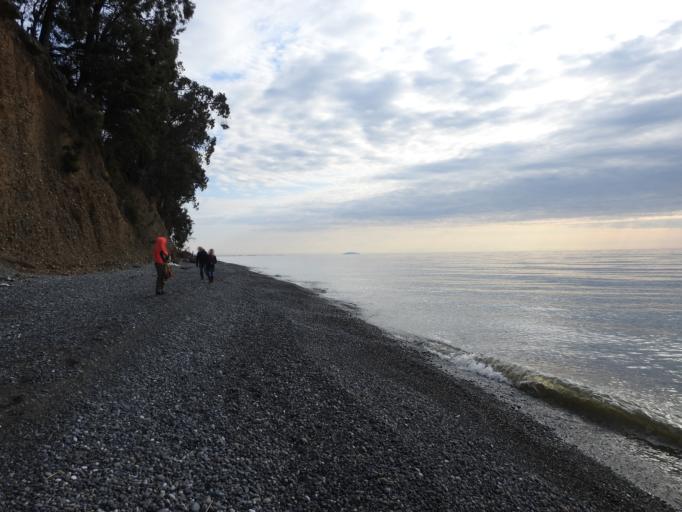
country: GE
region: Abkhazia
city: Dranda
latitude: 42.7935
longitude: 41.2547
